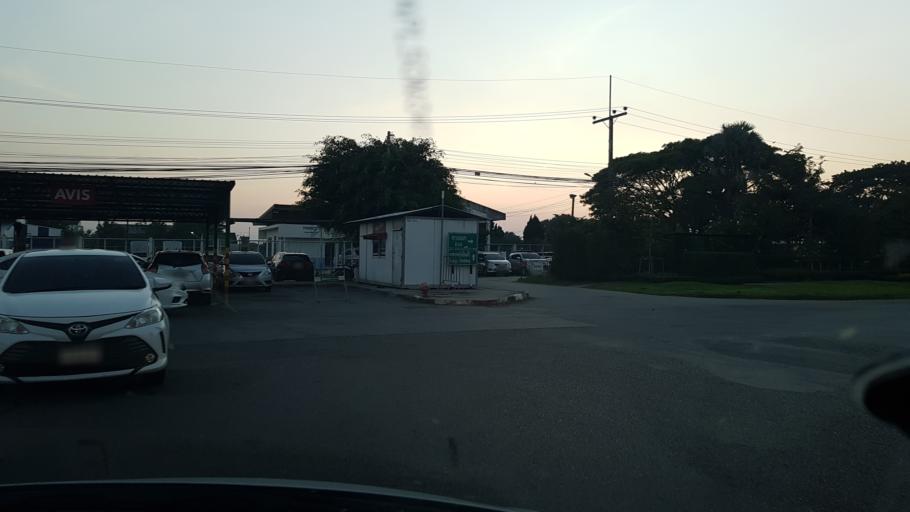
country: TH
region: Chiang Rai
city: Chiang Rai
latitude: 19.9539
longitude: 99.8786
